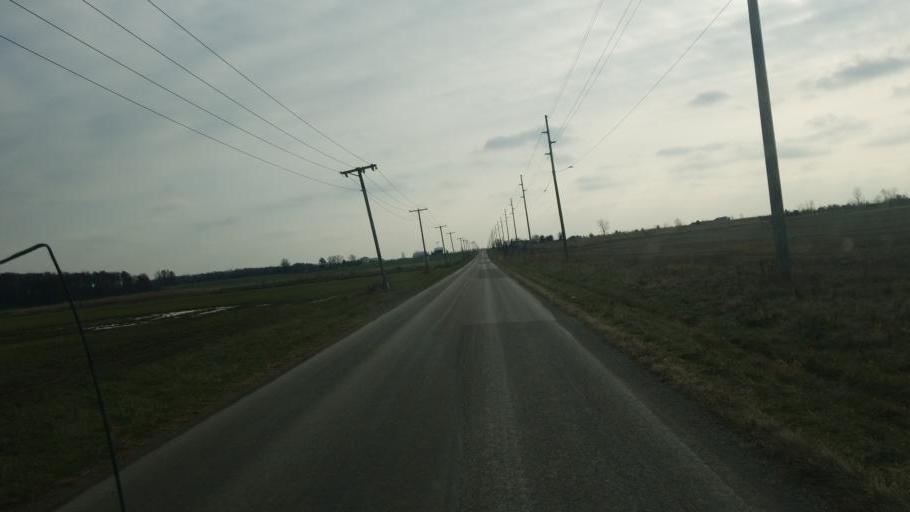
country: US
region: Indiana
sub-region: Adams County
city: Berne
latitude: 40.6417
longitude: -84.9643
